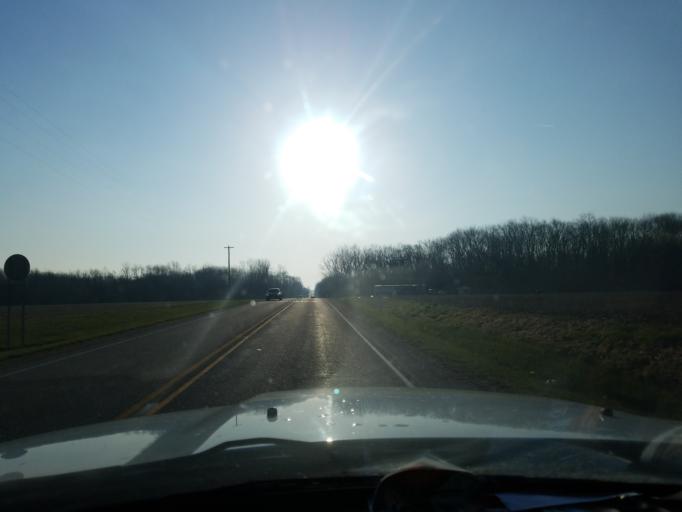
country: US
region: Indiana
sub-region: Vigo County
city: Seelyville
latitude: 39.3903
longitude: -87.2676
